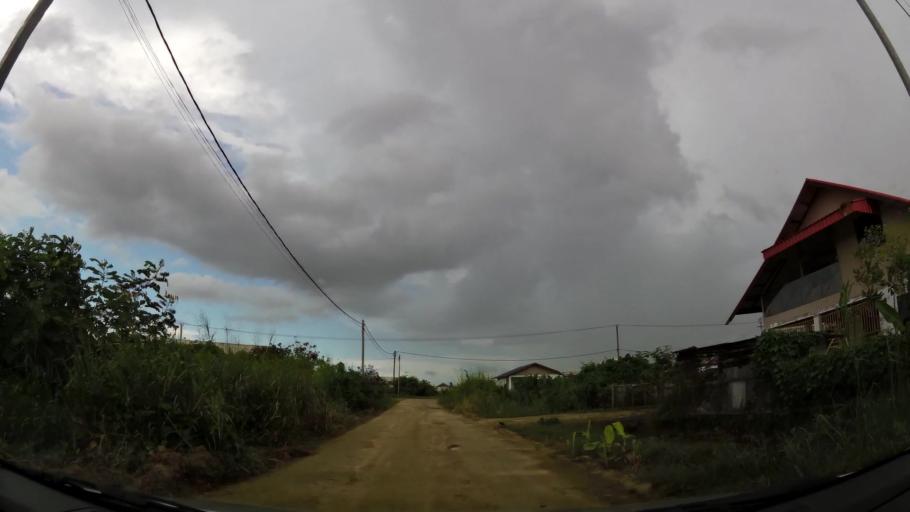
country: SR
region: Commewijne
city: Nieuw Amsterdam
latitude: 5.8518
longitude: -55.1160
